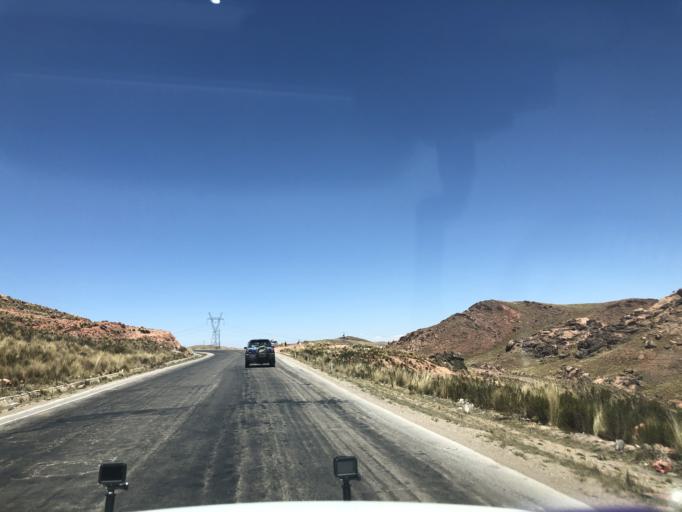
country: BO
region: Cochabamba
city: Colchani
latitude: -17.6960
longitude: -66.6993
